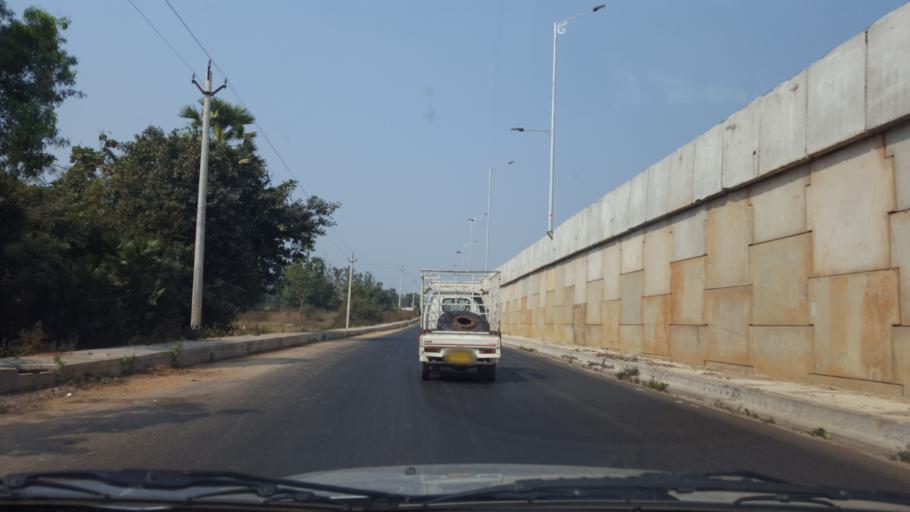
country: IN
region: Andhra Pradesh
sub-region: Vishakhapatnam
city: Bhimunipatnam
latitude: 17.8882
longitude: 83.3514
